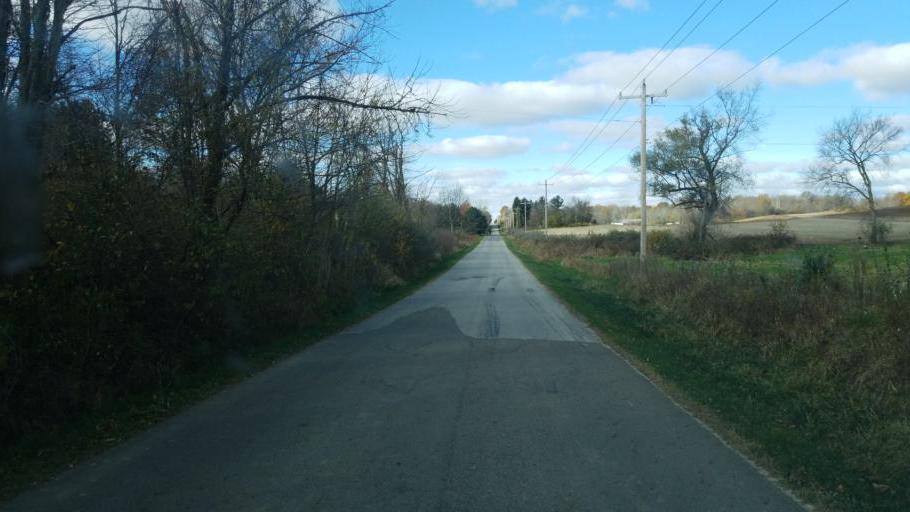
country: US
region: Ohio
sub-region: Crawford County
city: Galion
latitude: 40.6388
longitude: -82.7317
